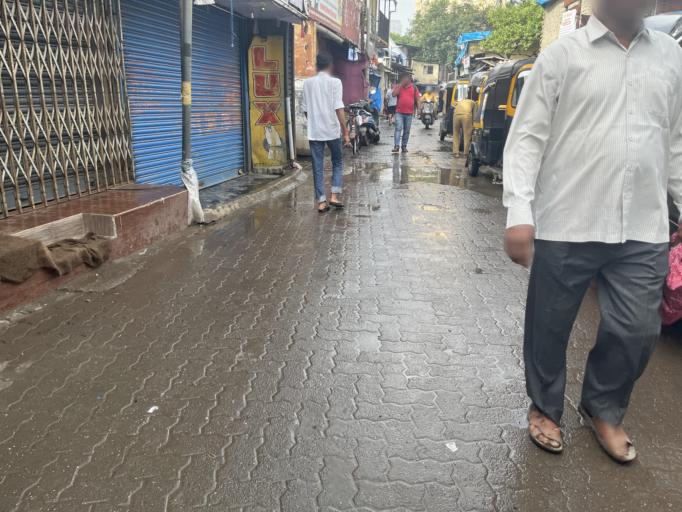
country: IN
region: Maharashtra
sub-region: Mumbai Suburban
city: Borivli
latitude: 19.2357
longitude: 72.8670
